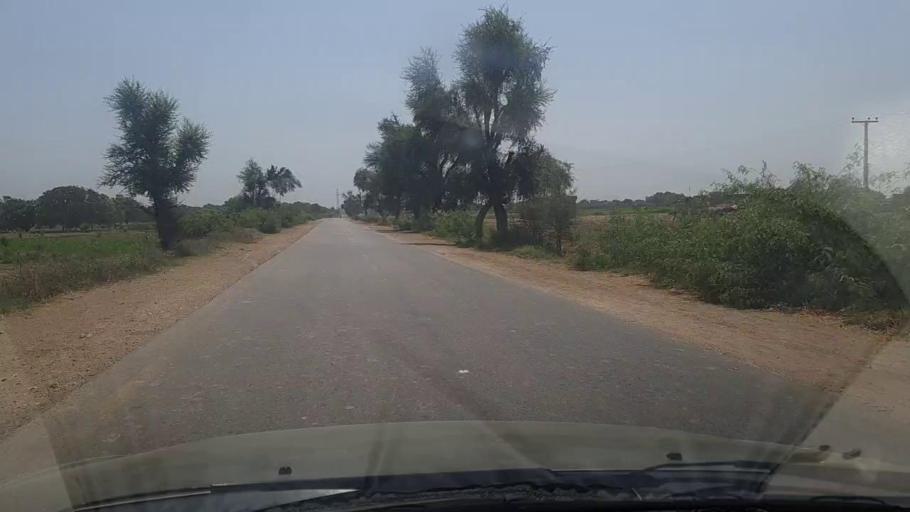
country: PK
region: Sindh
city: Tando Jam
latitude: 25.3623
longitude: 68.4909
